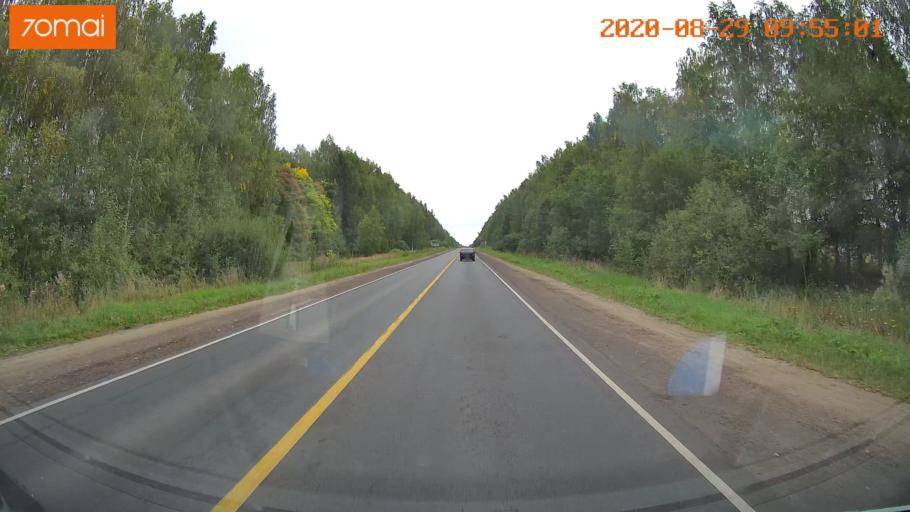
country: RU
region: Ivanovo
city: Zarechnyy
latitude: 57.4229
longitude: 42.2525
